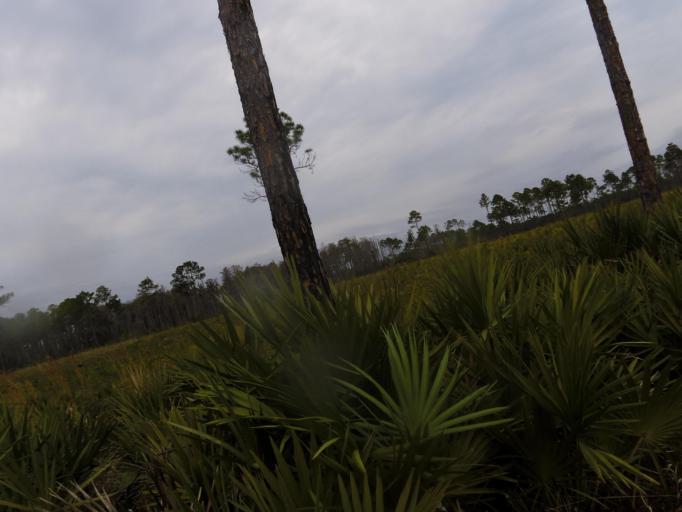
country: US
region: Florida
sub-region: Duval County
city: Atlantic Beach
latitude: 30.4706
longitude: -81.5002
